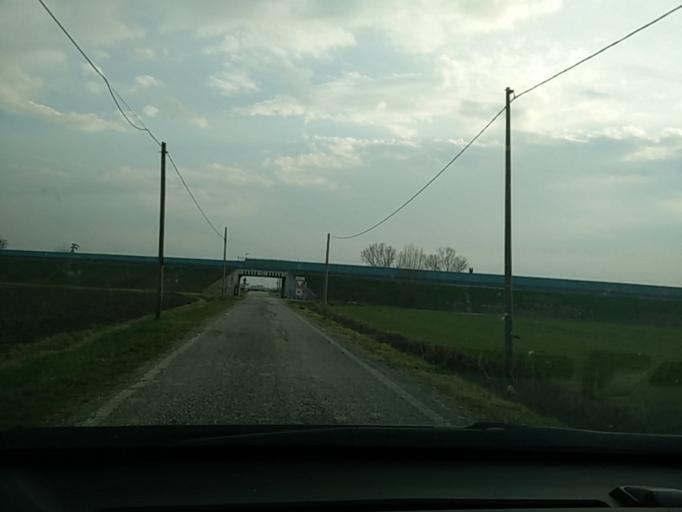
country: IT
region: Veneto
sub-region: Provincia di Venezia
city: Fossalta di Piave
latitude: 45.6092
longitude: 12.5067
